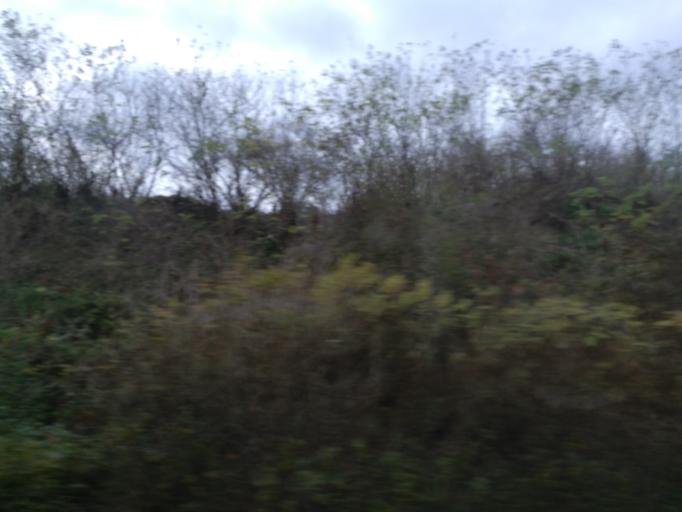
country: RO
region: Iasi
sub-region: Comuna Stolniceni-Prajescu
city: Stolniceni-Prajescu
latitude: 47.2055
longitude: 26.7409
